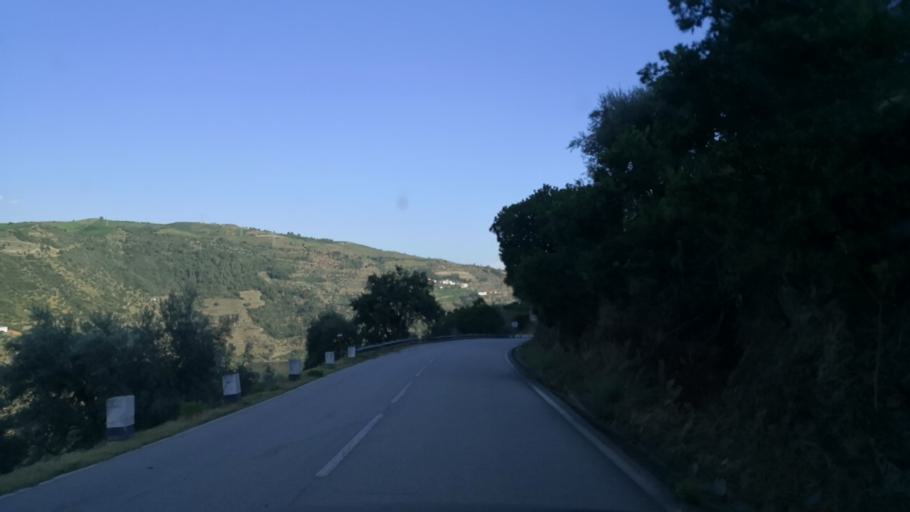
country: PT
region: Viseu
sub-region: Sao Joao da Pesqueira
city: Sao Joao da Pesqueira
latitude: 41.2362
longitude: -7.4305
